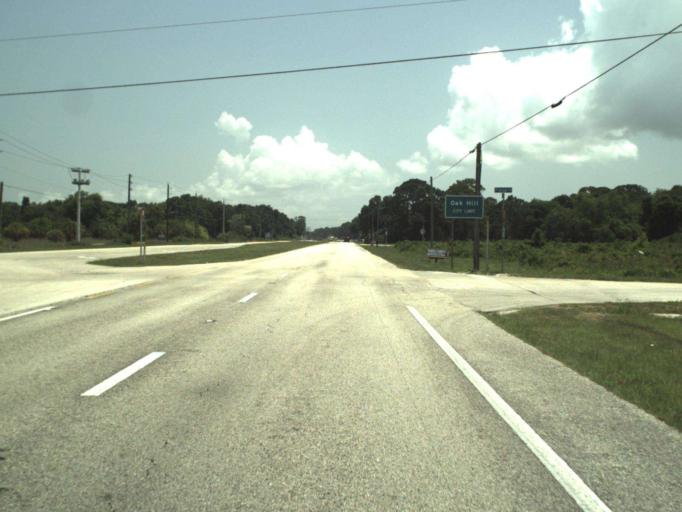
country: US
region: Florida
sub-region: Volusia County
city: Oak Hill
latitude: 28.9010
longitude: -80.8638
